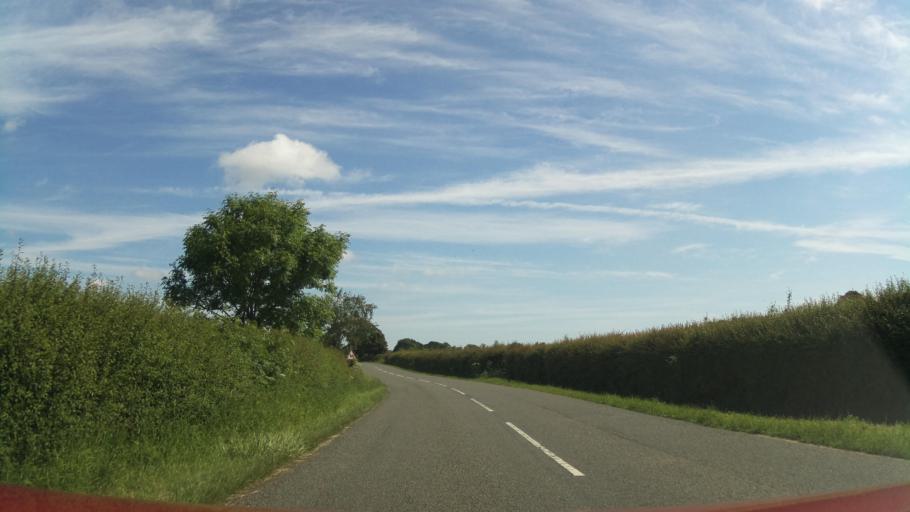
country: GB
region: England
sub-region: Lincolnshire
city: Skellingthorpe
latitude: 53.1449
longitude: -0.6325
